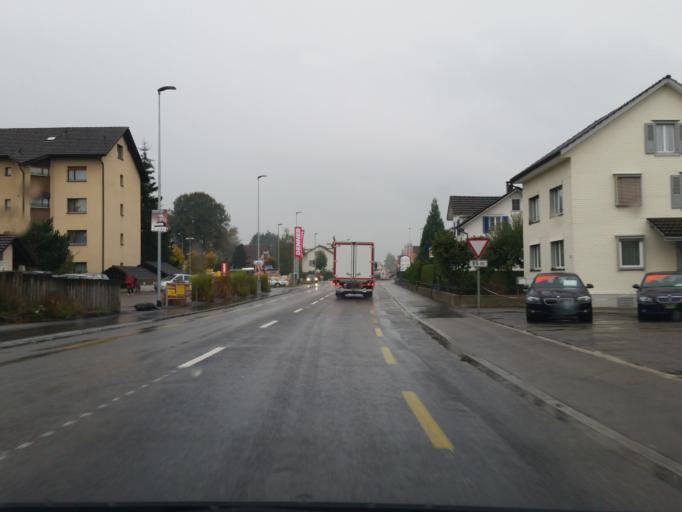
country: CH
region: Thurgau
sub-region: Arbon District
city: Amriswil
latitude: 47.5444
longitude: 9.2874
